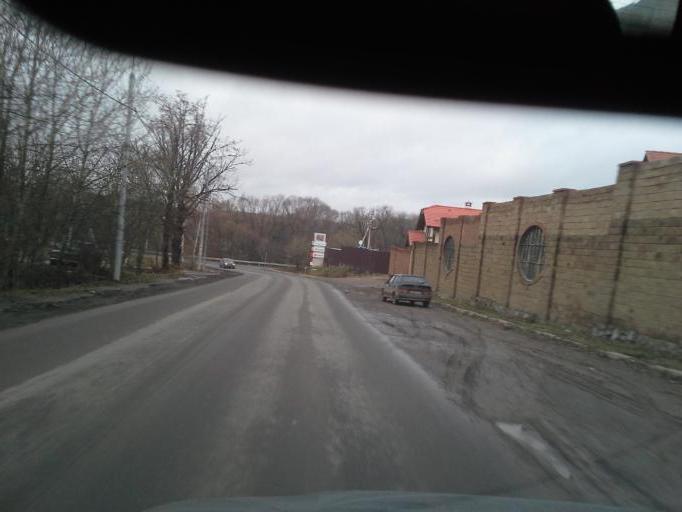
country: RU
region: Moskovskaya
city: Moskovskiy
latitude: 55.5708
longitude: 37.3925
